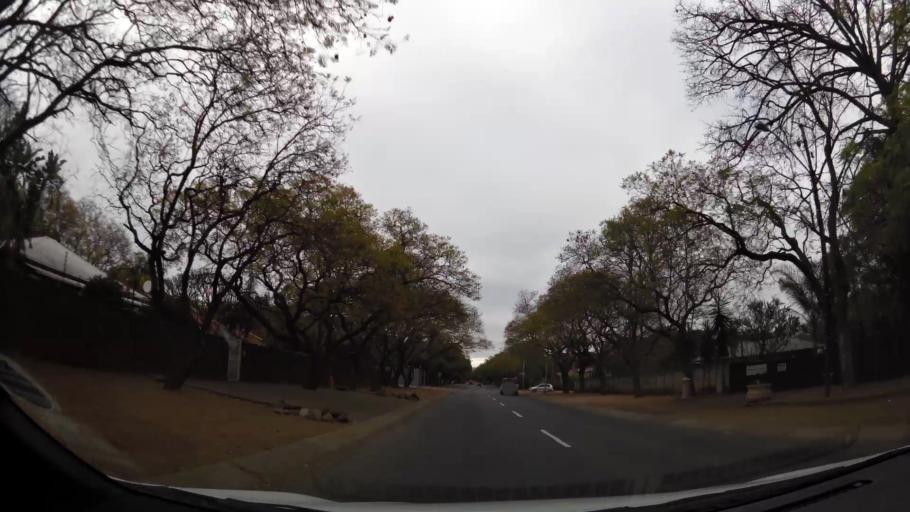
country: ZA
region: Limpopo
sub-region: Capricorn District Municipality
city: Polokwane
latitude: -23.9016
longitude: 29.4674
